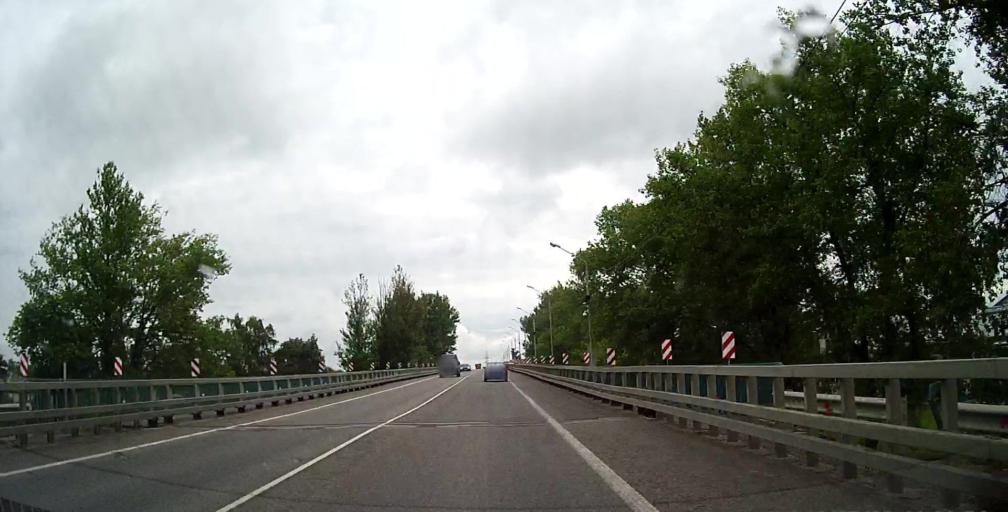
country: RU
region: Smolensk
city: Katyn'
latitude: 54.7820
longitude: 31.8192
